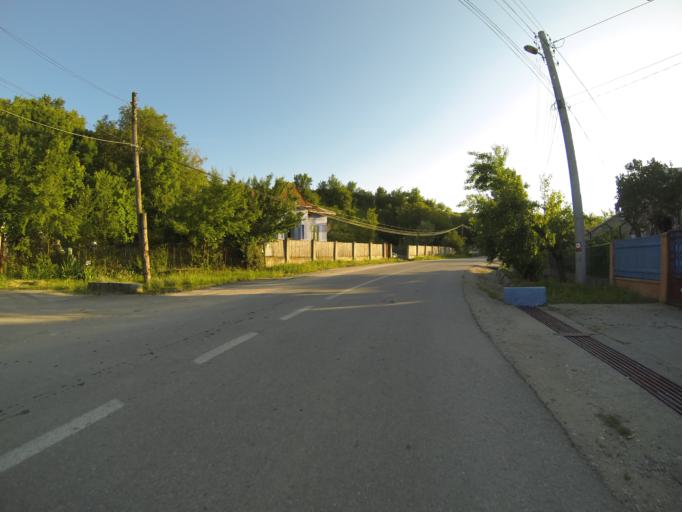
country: RO
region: Dolj
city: Satu Nou Calopar
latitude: 44.1594
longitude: 23.7948
